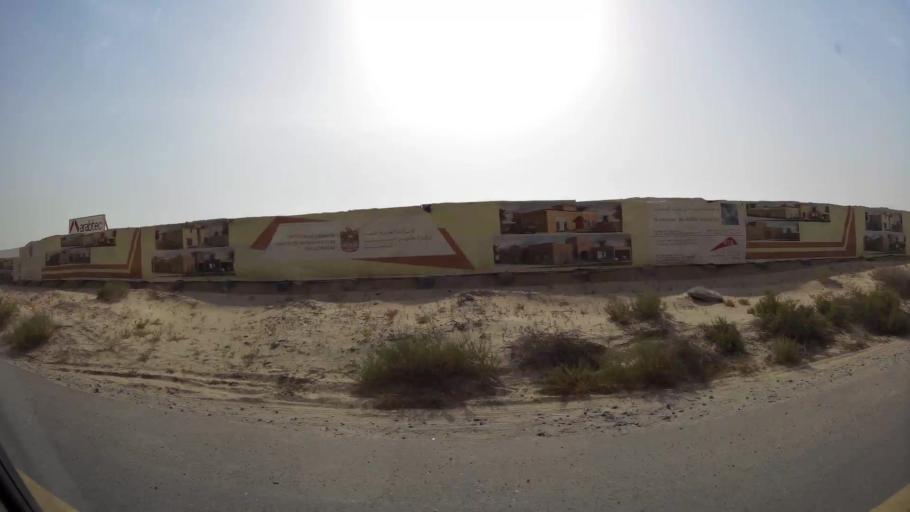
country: AE
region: Ash Shariqah
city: Sharjah
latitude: 25.2608
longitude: 55.4562
